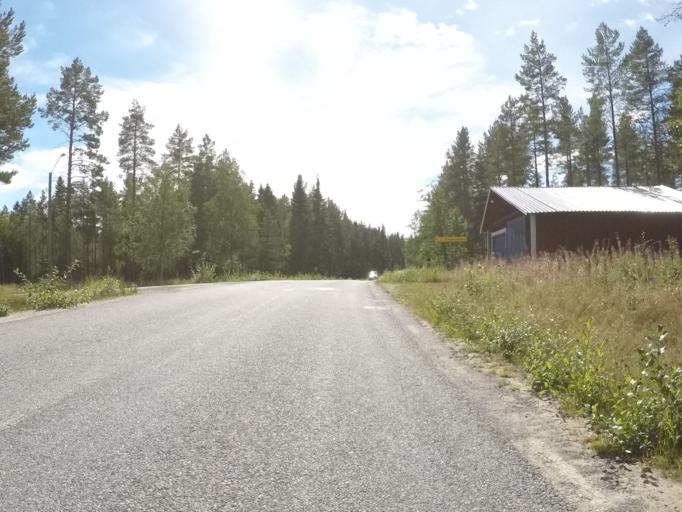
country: SE
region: Vaesterbotten
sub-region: Robertsfors Kommun
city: Robertsfors
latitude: 63.9612
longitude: 20.8085
